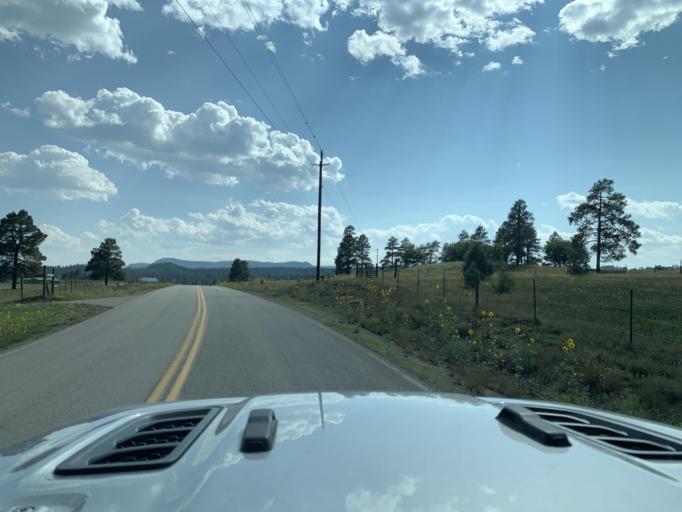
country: US
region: Colorado
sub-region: Archuleta County
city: Pagosa Springs
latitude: 37.2443
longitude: -107.0338
